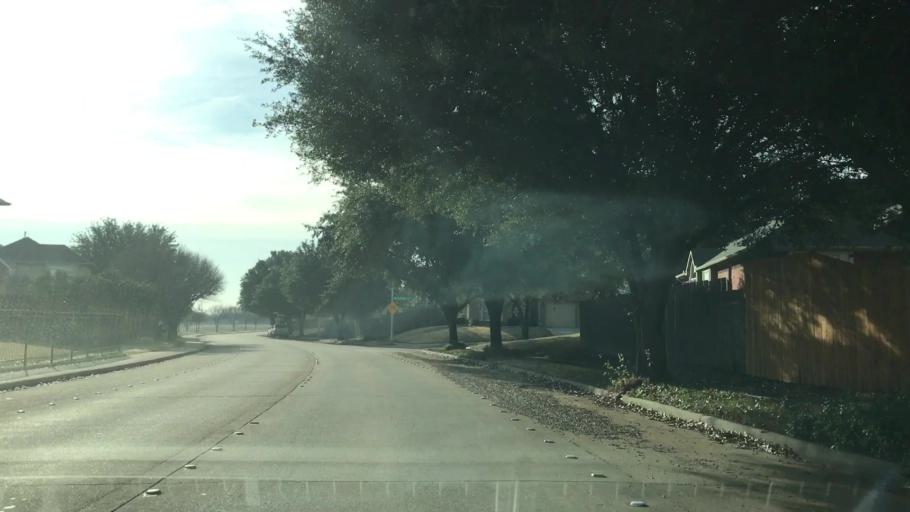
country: US
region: Texas
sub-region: Tarrant County
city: Watauga
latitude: 32.8755
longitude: -97.2797
